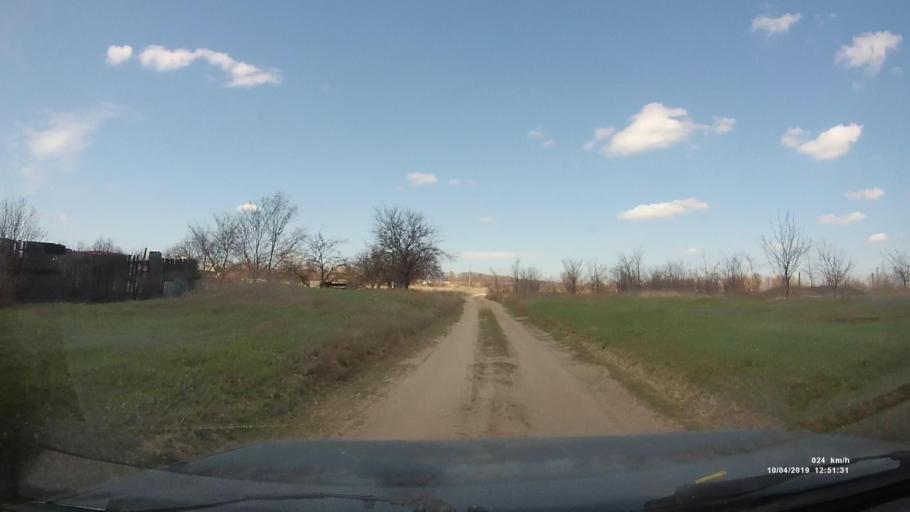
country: RU
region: Rostov
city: Kamensk-Shakhtinskiy
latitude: 48.3597
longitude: 40.2169
